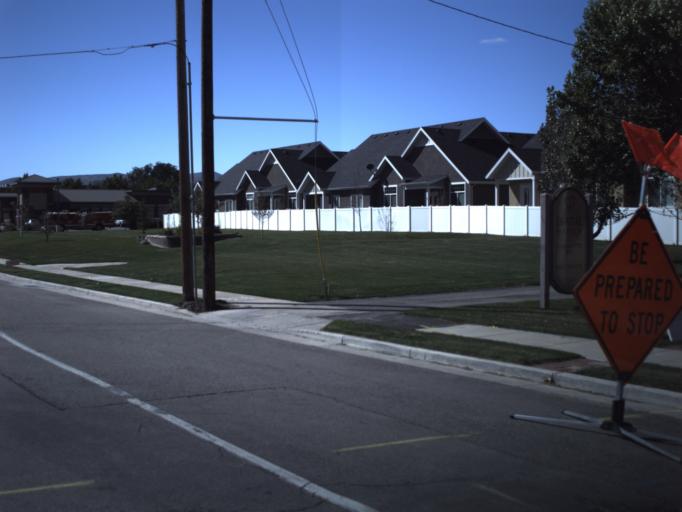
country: US
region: Utah
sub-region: Salt Lake County
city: Riverton
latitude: 40.5207
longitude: -111.9388
